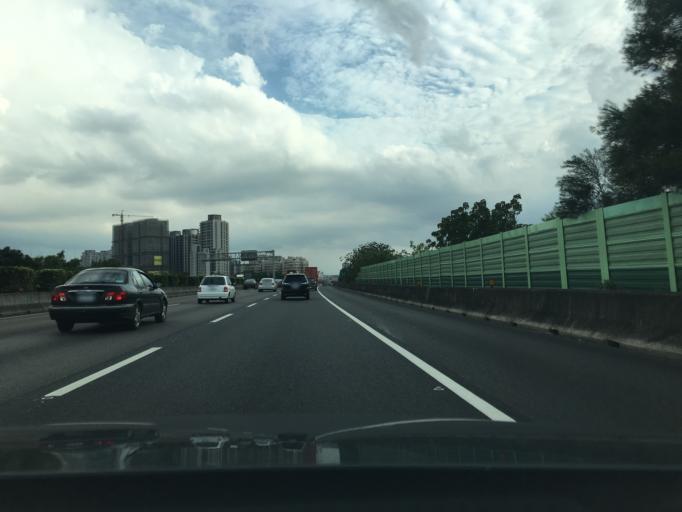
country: TW
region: Taiwan
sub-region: Hsinchu
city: Zhubei
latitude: 24.8399
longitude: 121.0223
